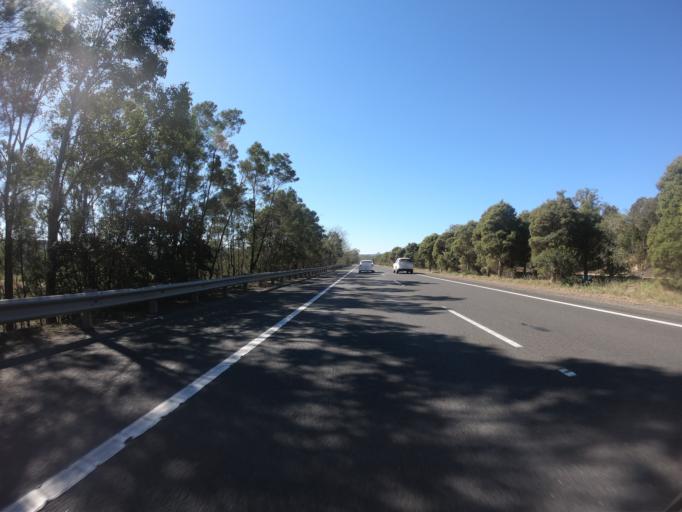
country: AU
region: New South Wales
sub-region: Wingecarribee
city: Bundanoon
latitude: -34.6761
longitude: 150.0602
